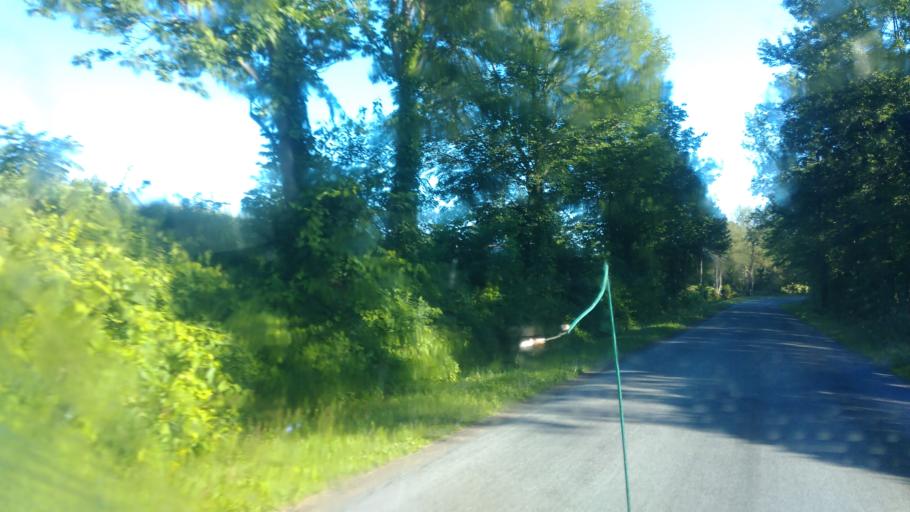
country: US
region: New York
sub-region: Wayne County
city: Lyons
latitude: 43.1284
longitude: -77.0386
